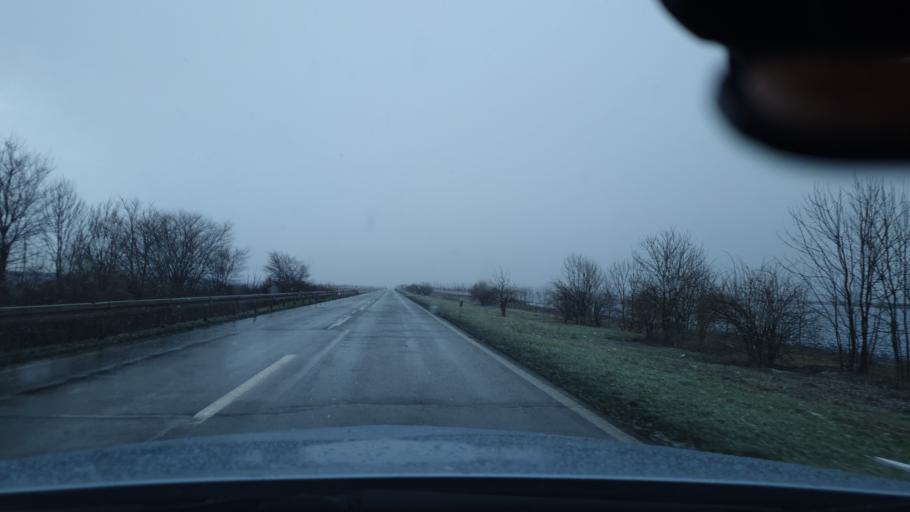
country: RS
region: Autonomna Pokrajina Vojvodina
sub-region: Juznobanatski Okrug
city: Pancevo
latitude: 44.8577
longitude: 20.7512
